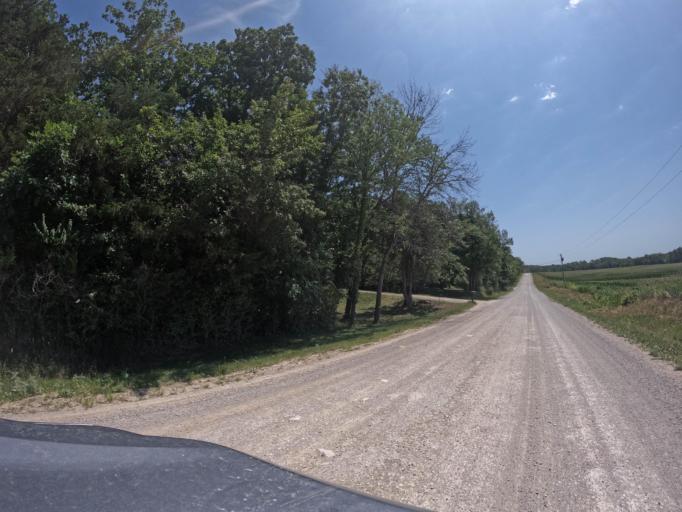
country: US
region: Iowa
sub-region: Henry County
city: Mount Pleasant
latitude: 40.8922
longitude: -91.5444
